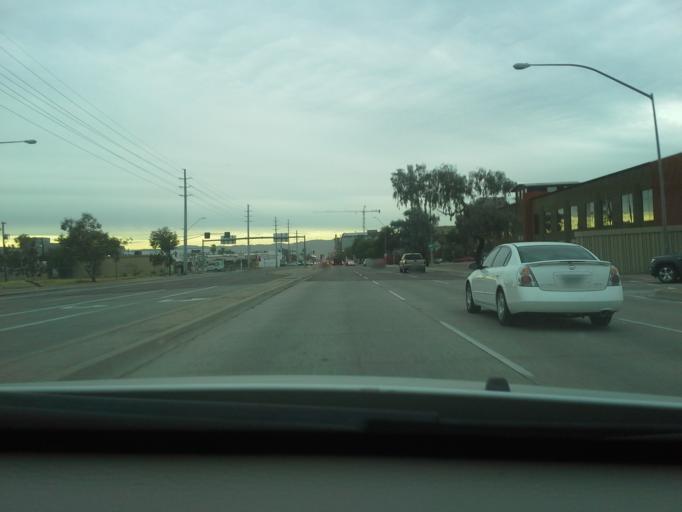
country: US
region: Arizona
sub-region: Maricopa County
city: Phoenix
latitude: 33.4617
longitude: -112.0653
